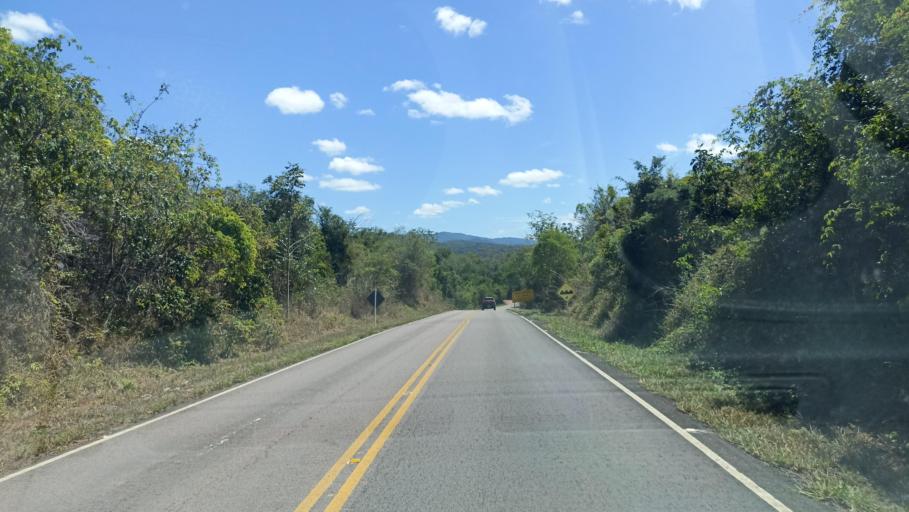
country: BR
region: Bahia
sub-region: Andarai
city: Vera Cruz
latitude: -12.7596
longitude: -41.3279
